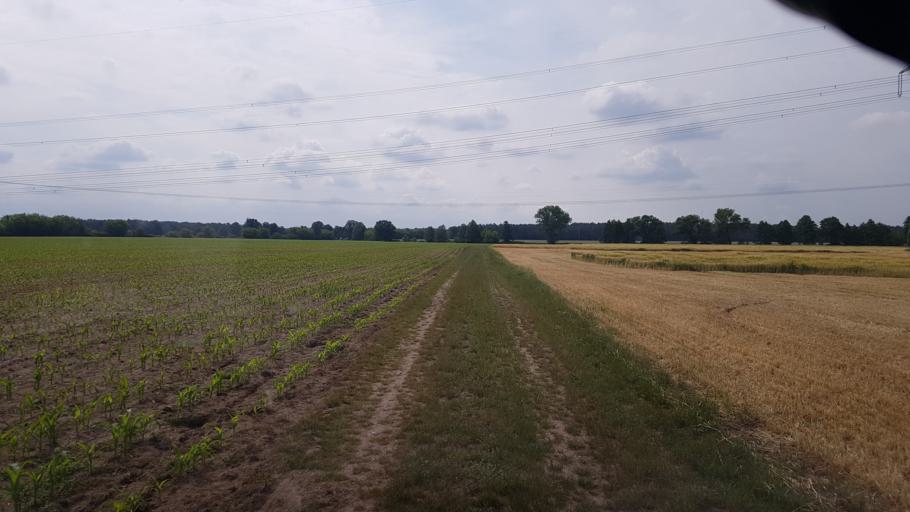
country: DE
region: Brandenburg
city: Schonewalde
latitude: 51.6537
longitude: 13.5939
